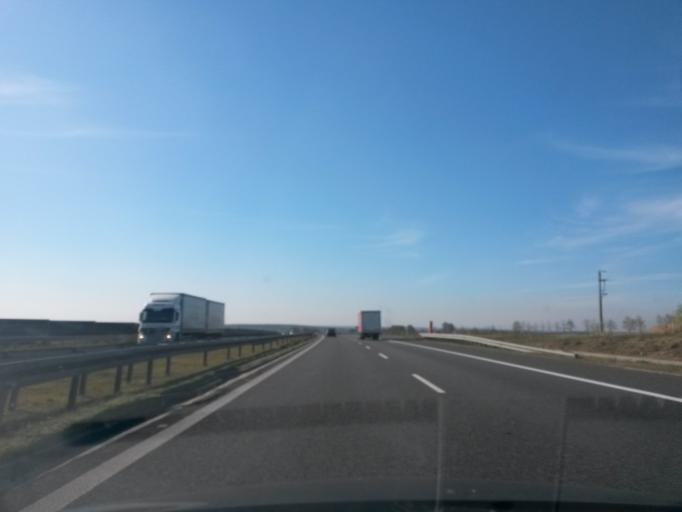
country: PL
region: Opole Voivodeship
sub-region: Powiat krapkowicki
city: Gogolin
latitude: 50.4827
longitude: 18.0503
